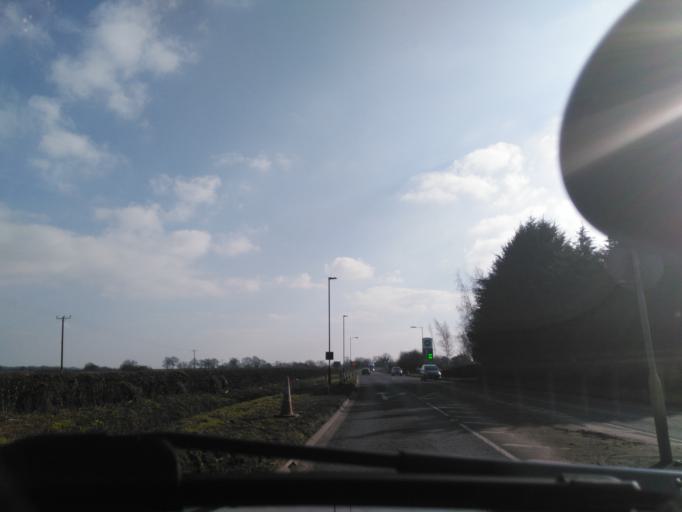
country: GB
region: England
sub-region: Wiltshire
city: Norton
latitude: 51.5252
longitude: -2.1232
